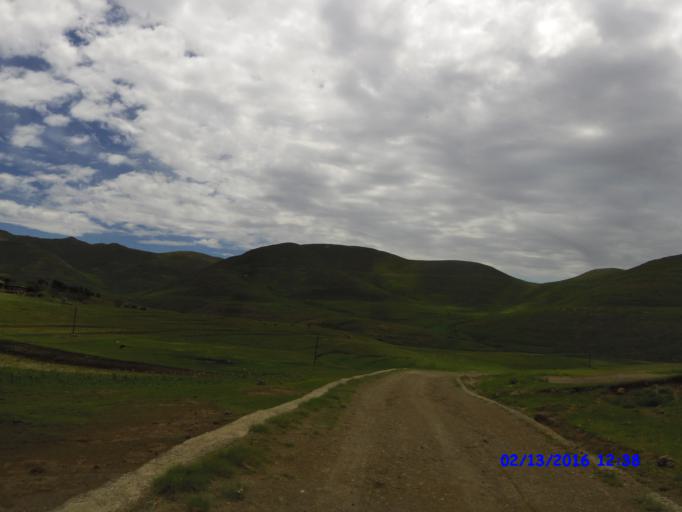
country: LS
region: Maseru
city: Nako
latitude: -29.8364
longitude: 28.0279
